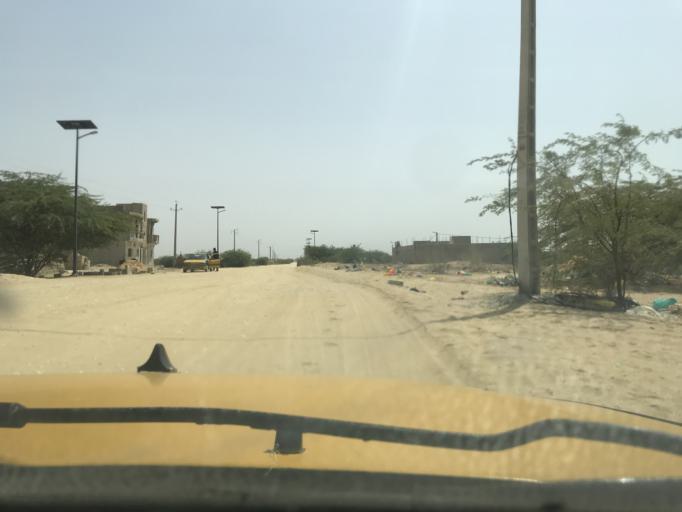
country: SN
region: Saint-Louis
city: Saint-Louis
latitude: 16.0334
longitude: -16.4444
